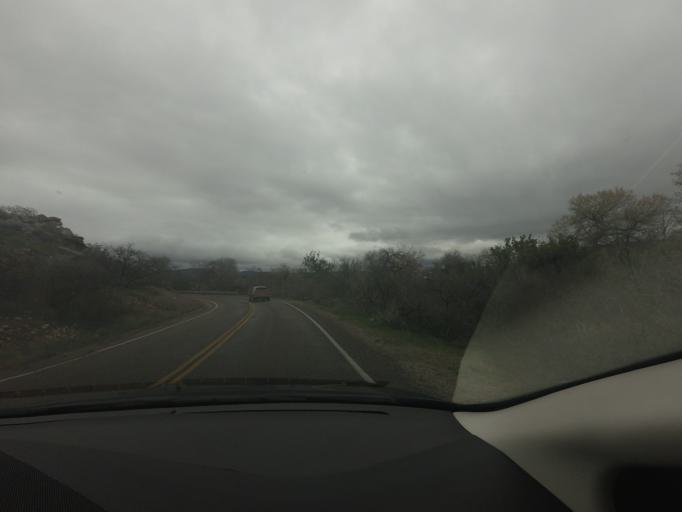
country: US
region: Arizona
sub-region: Yavapai County
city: Lake Montezuma
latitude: 34.6480
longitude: -111.7651
